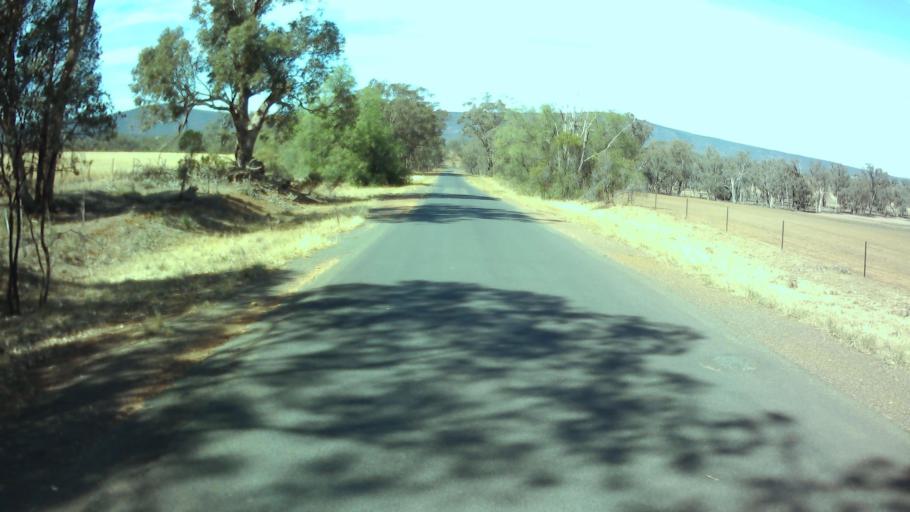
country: AU
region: New South Wales
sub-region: Weddin
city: Grenfell
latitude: -33.9356
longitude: 148.0822
